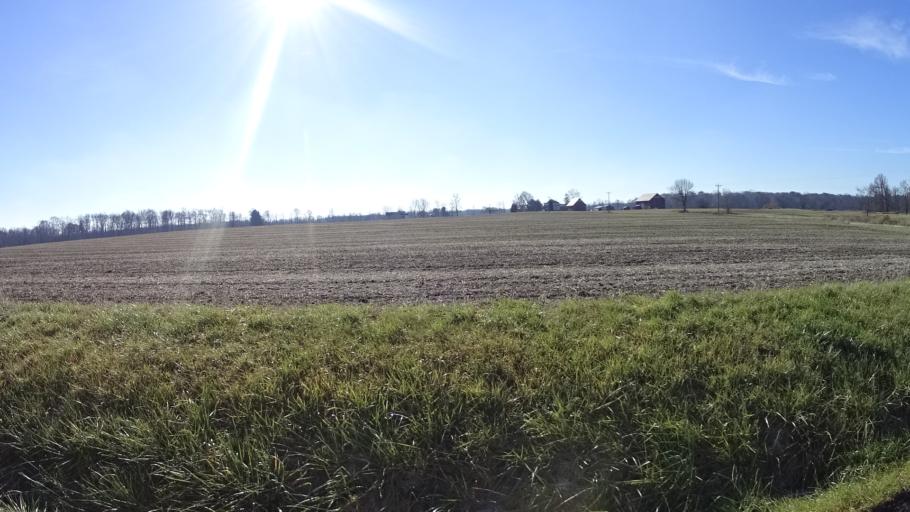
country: US
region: Ohio
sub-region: Huron County
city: New London
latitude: 41.1296
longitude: -82.3295
